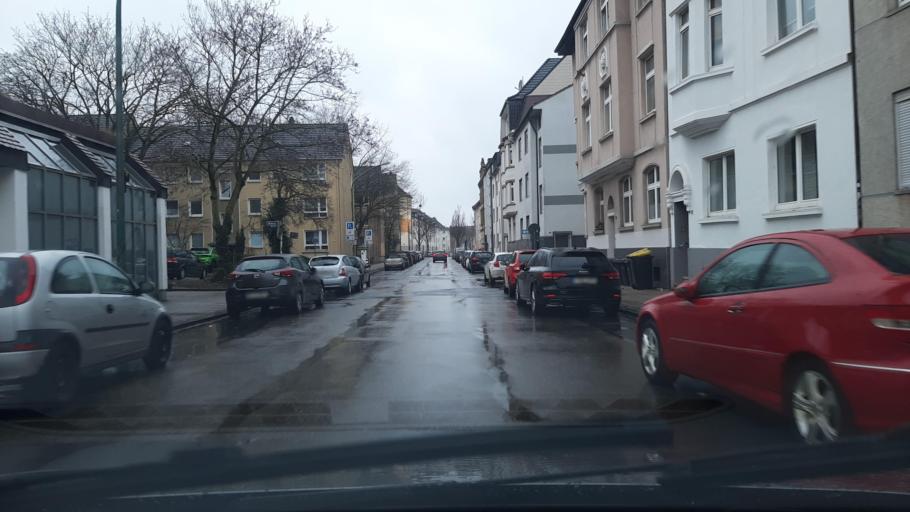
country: DE
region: North Rhine-Westphalia
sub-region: Regierungsbezirk Dusseldorf
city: Essen
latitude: 51.4442
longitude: 6.9761
